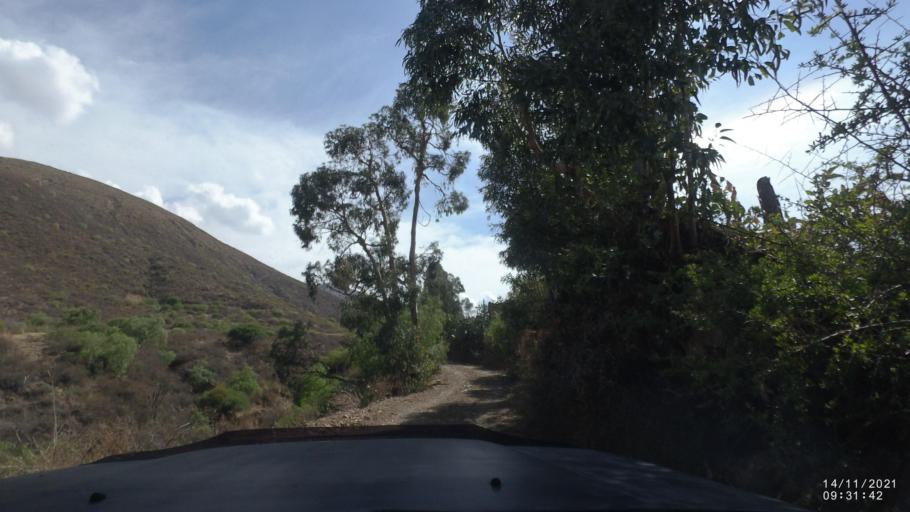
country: BO
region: Cochabamba
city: Cochabamba
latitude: -17.3685
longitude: -66.0900
